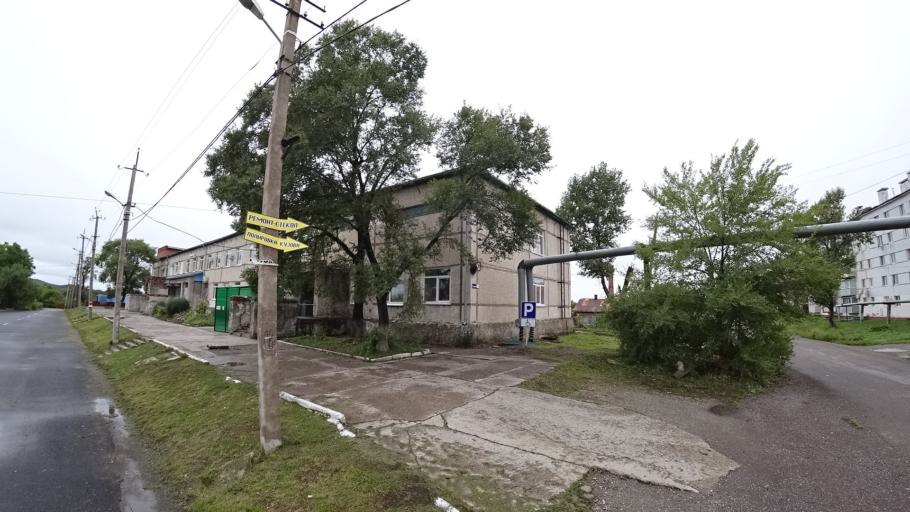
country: RU
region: Primorskiy
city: Monastyrishche
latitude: 44.2021
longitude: 132.4470
